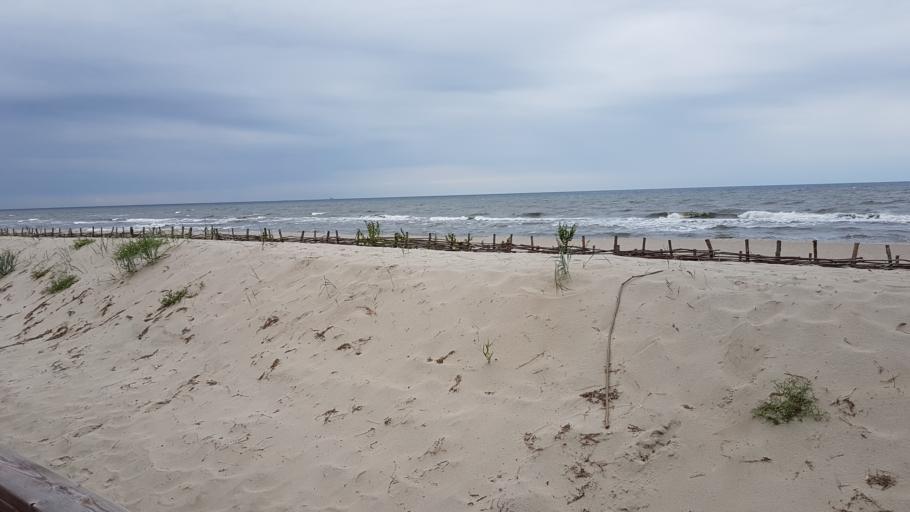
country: RU
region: Kaliningrad
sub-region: Gorod Kaliningrad
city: Yantarnyy
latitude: 54.8746
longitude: 19.9328
